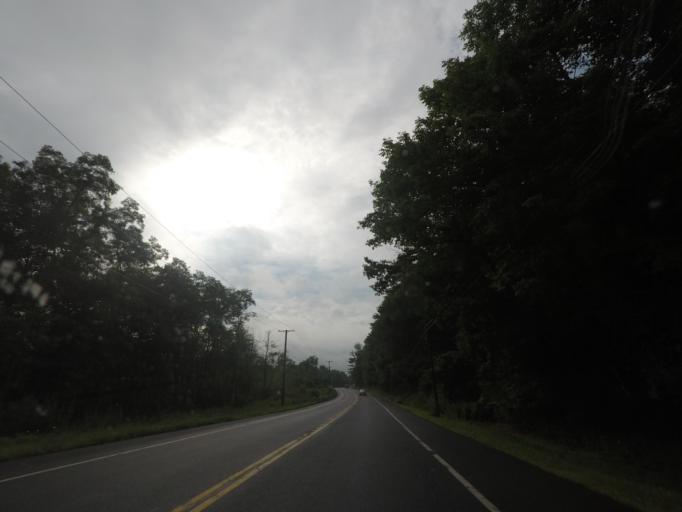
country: US
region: New York
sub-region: Rensselaer County
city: Nassau
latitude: 42.5108
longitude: -73.5674
